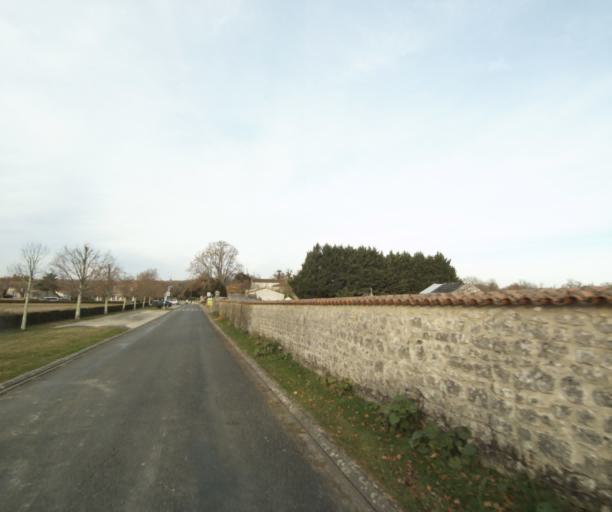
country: FR
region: Poitou-Charentes
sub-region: Departement de la Charente-Maritime
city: Saint-Hilaire-de-Villefranche
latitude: 45.8174
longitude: -0.5693
